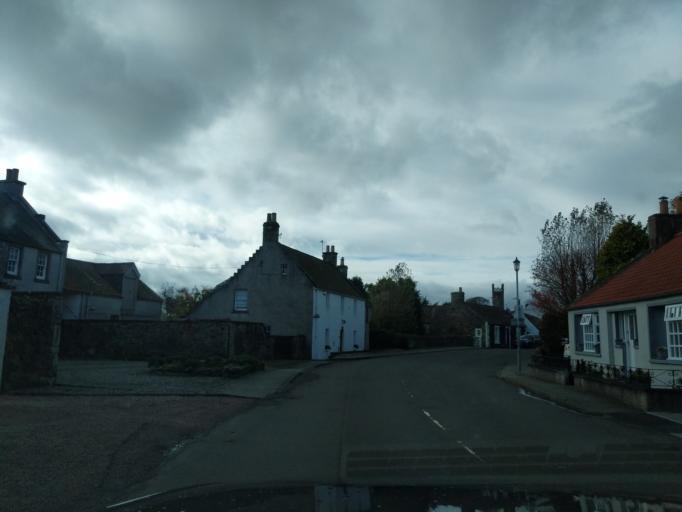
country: GB
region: Scotland
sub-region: Fife
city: Saint Monance
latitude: 56.2086
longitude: -2.8268
